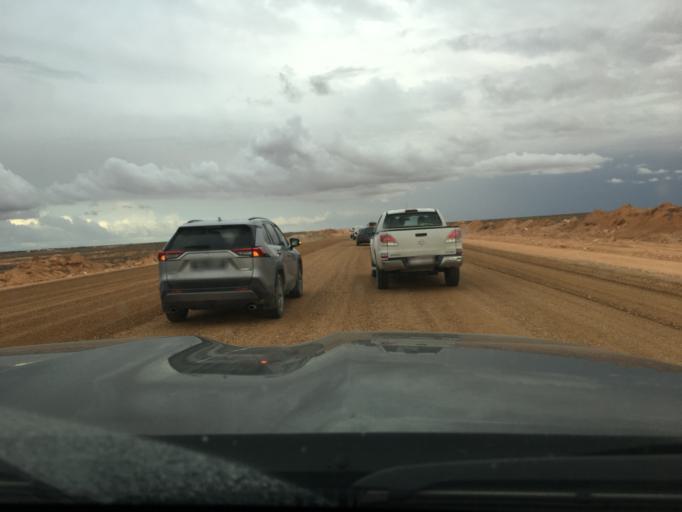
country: TN
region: Madanin
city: Medenine
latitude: 33.2657
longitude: 10.5822
